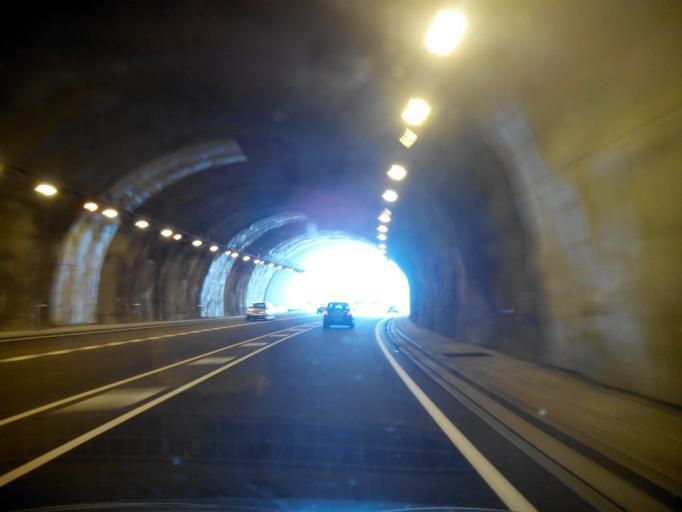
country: ES
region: Catalonia
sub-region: Provincia de Barcelona
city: Castelloli
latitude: 41.6139
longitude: 1.6808
